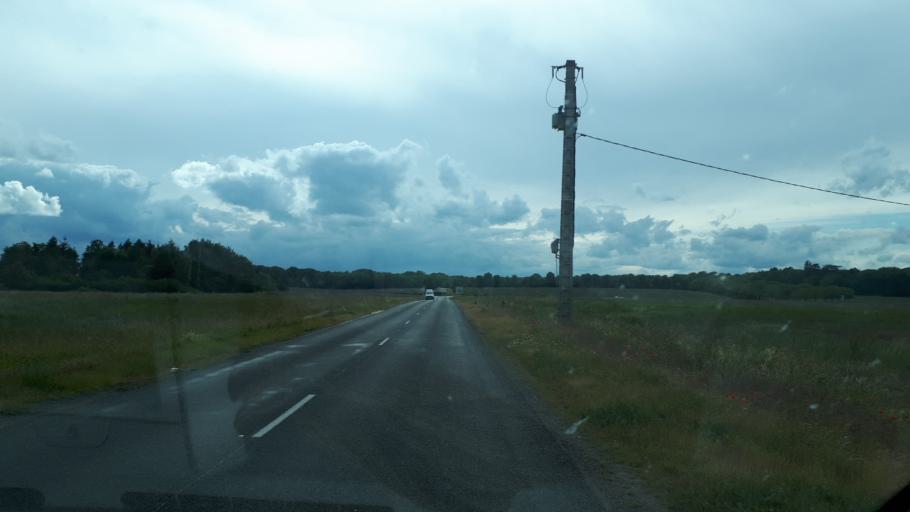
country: FR
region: Centre
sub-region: Departement du Cher
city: Mehun-sur-Yevre
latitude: 47.0786
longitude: 2.1854
